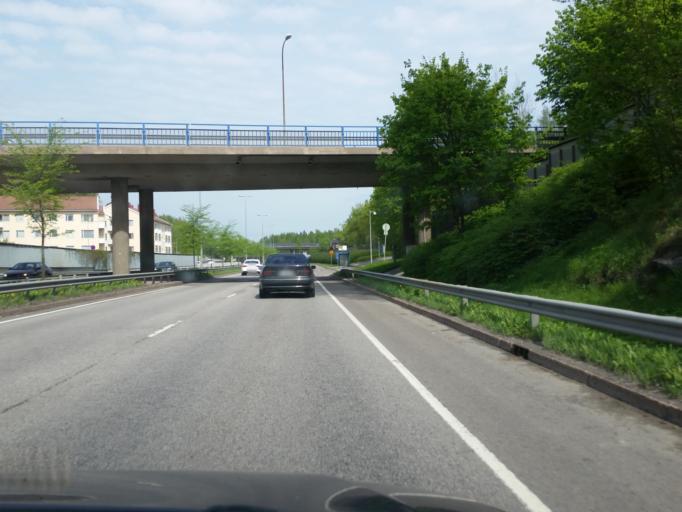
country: FI
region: Uusimaa
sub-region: Helsinki
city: Helsinki
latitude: 60.2117
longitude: 24.9013
